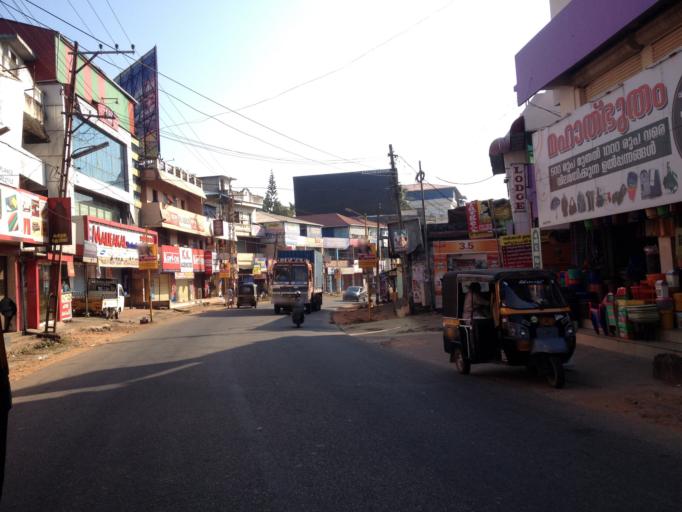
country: IN
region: Kerala
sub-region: Kollam
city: Punalur
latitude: 9.0056
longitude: 76.7757
